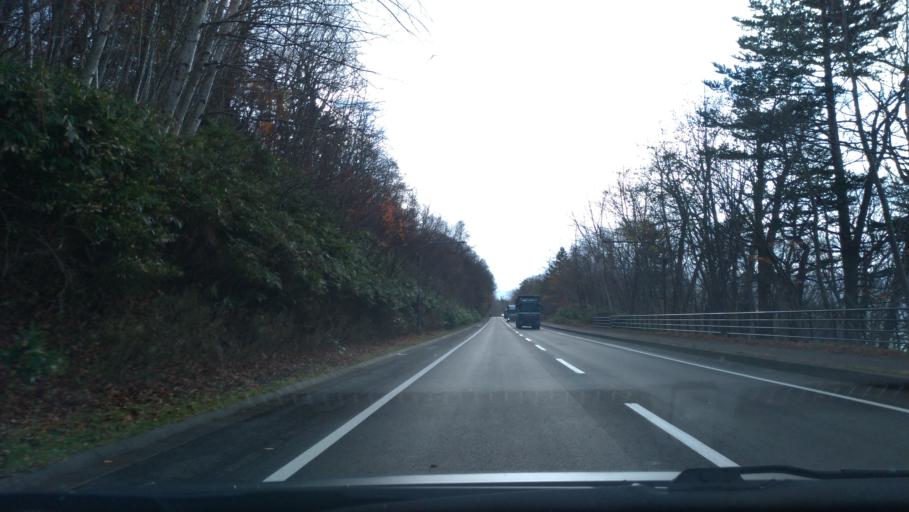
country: JP
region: Hokkaido
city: Shiraoi
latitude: 42.7222
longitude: 141.3301
